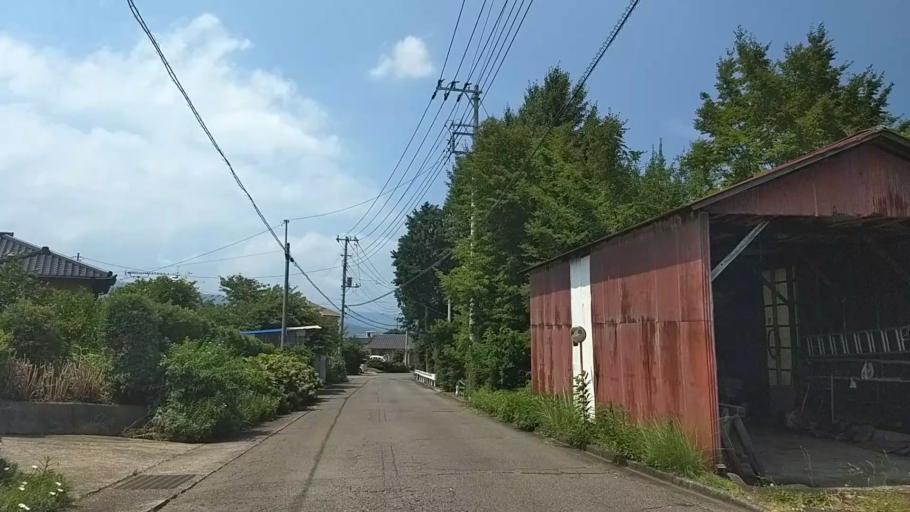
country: JP
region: Shizuoka
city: Ito
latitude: 34.9461
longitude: 139.1051
